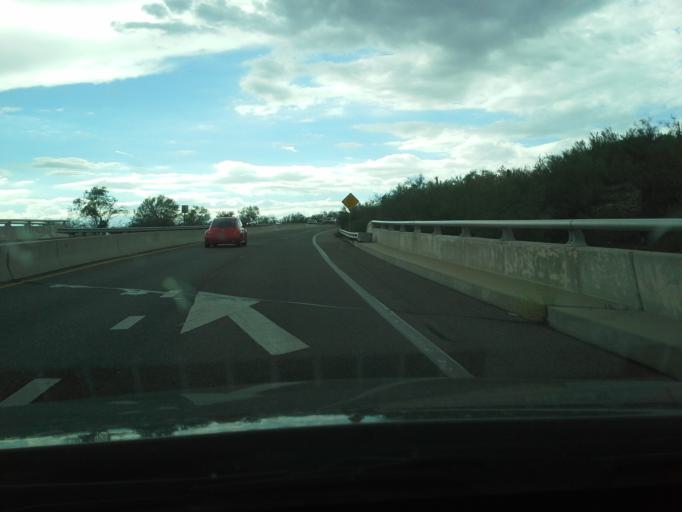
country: US
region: Arizona
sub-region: Pima County
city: South Tucson
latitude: 32.2056
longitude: -110.9932
